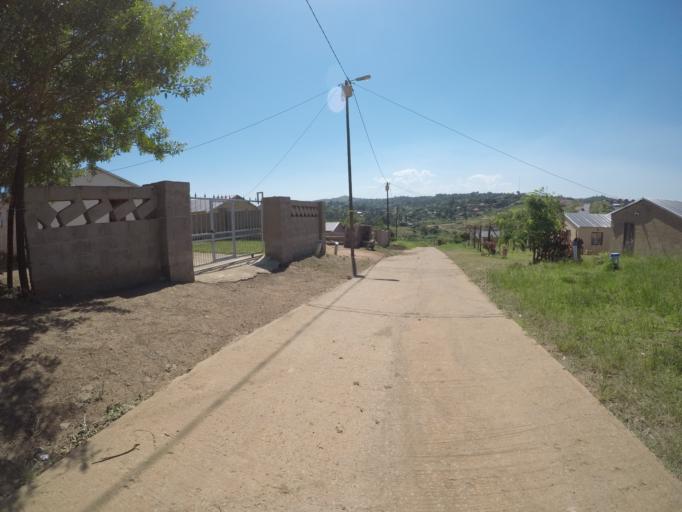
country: ZA
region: KwaZulu-Natal
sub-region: uThungulu District Municipality
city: Empangeni
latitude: -28.7676
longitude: 31.8768
